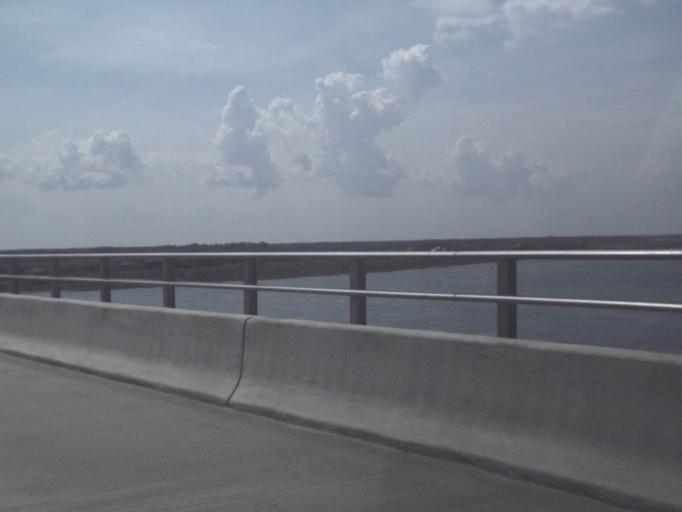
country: US
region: Florida
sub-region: Saint Johns County
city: Villano Beach
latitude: 29.9178
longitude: -81.3010
